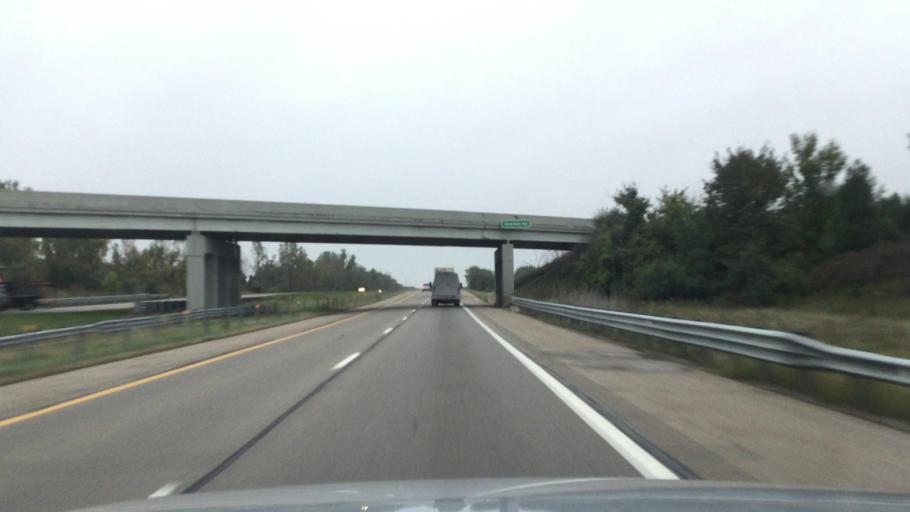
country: US
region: Michigan
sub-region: Shiawassee County
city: Durand
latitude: 42.9515
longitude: -83.9737
